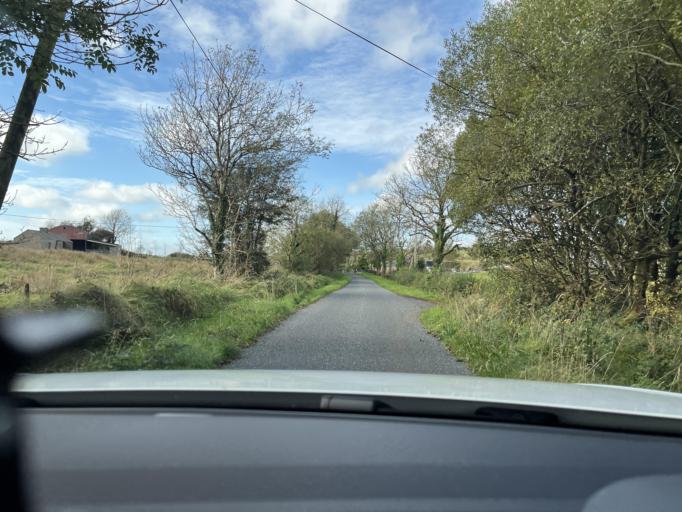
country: IE
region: Connaught
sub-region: Sligo
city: Ballymote
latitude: 54.0760
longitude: -8.4388
